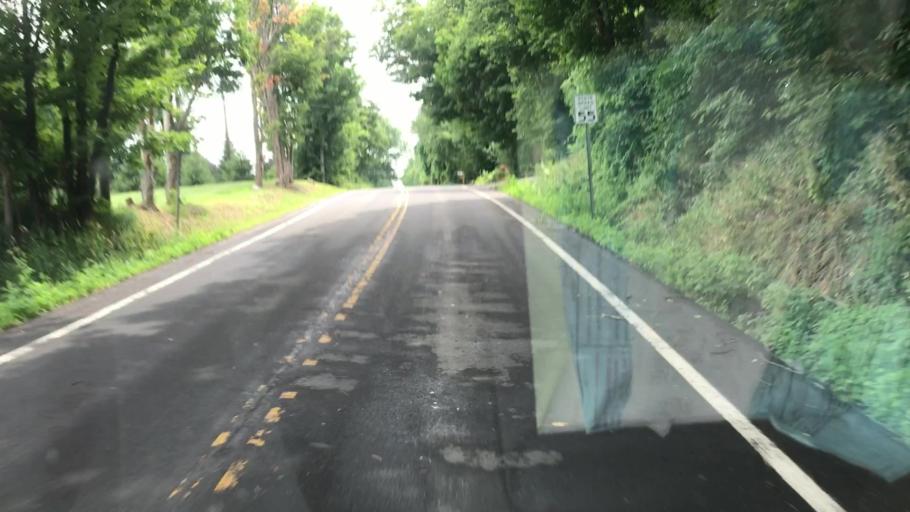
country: US
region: New York
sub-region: Onondaga County
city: Manlius
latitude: 42.9430
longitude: -75.9794
